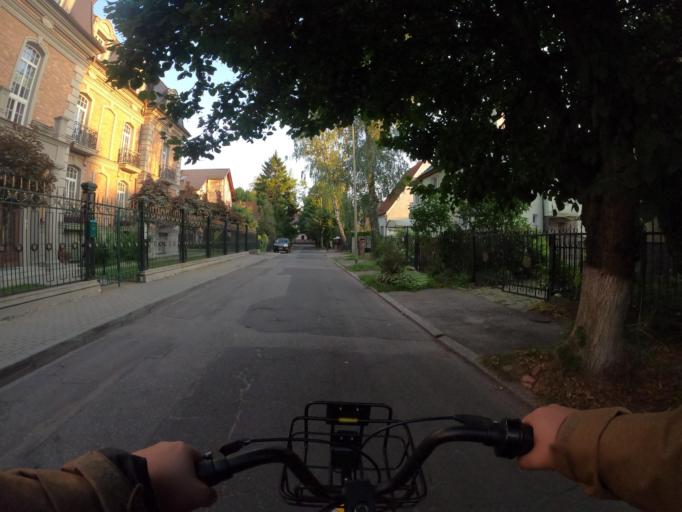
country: RU
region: Kaliningrad
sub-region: Gorod Kaliningrad
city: Kaliningrad
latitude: 54.7186
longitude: 20.4609
